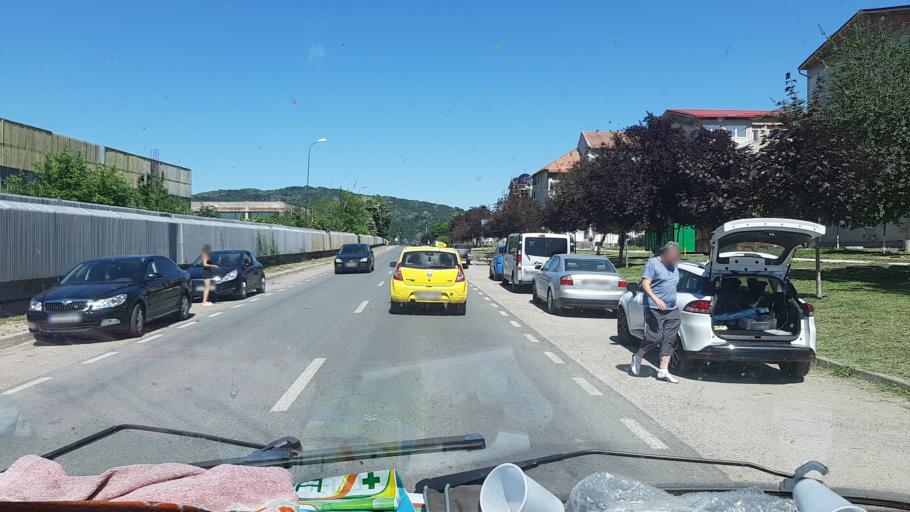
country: RO
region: Caras-Severin
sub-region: Oras Bocsa
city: Bocsa
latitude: 45.3778
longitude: 21.7233
